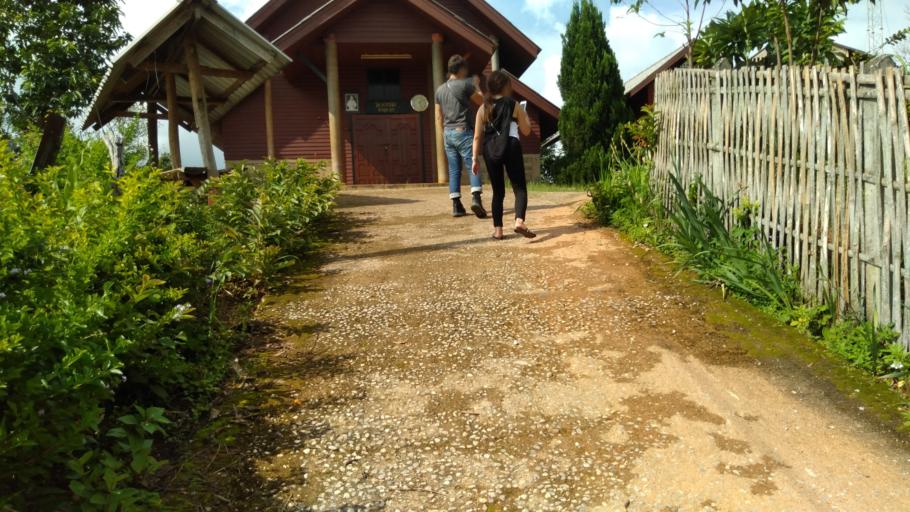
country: TH
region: Chiang Mai
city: Phrao
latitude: 19.5106
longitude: 99.3381
